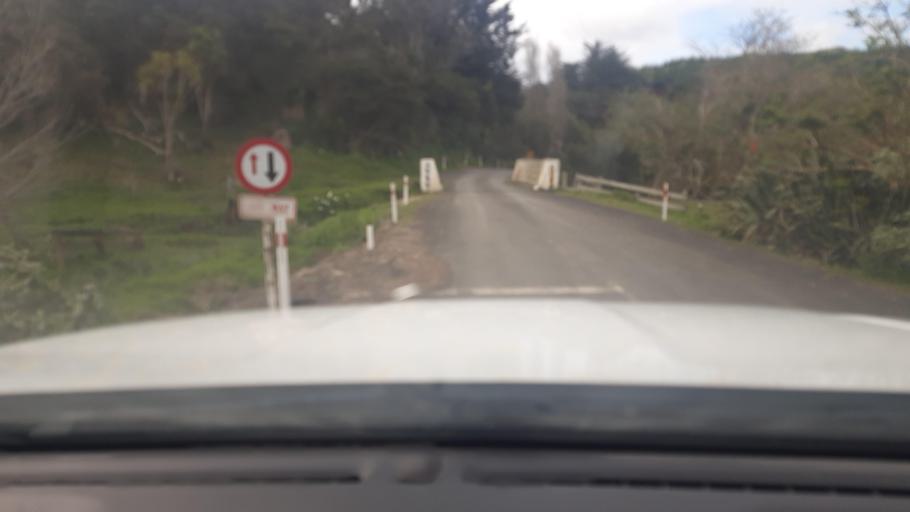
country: NZ
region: Northland
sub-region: Far North District
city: Ahipara
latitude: -35.2905
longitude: 173.2069
